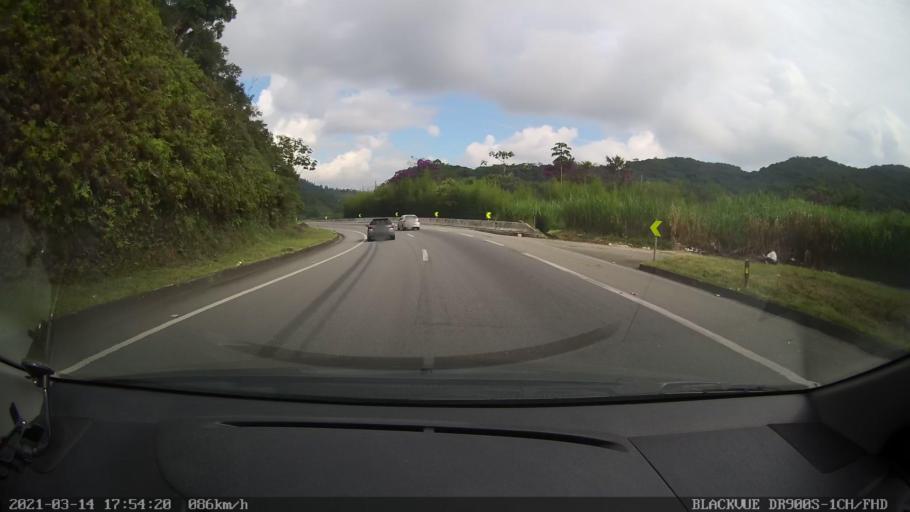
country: BR
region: Rio de Janeiro
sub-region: Petropolis
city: Petropolis
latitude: -22.4859
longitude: -43.2270
